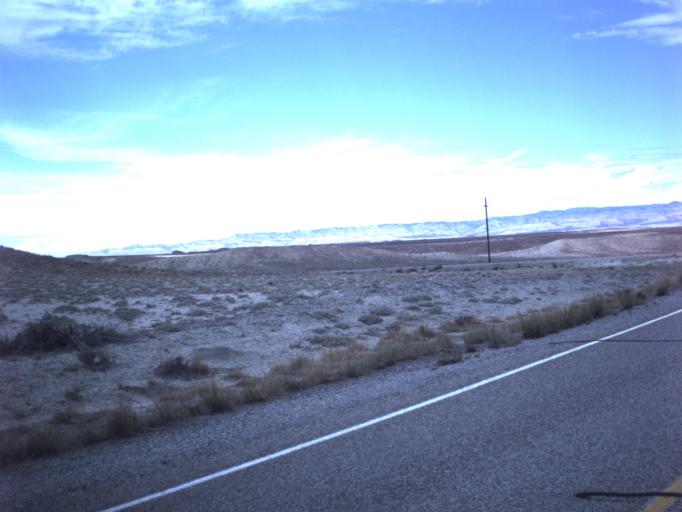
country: US
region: Utah
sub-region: Grand County
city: Moab
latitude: 38.9361
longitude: -109.3466
